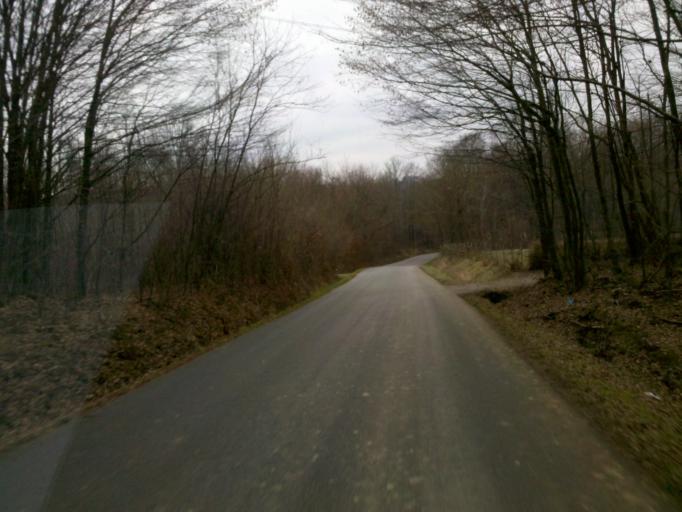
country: HR
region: Grad Zagreb
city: Horvati
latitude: 45.6736
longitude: 15.8295
